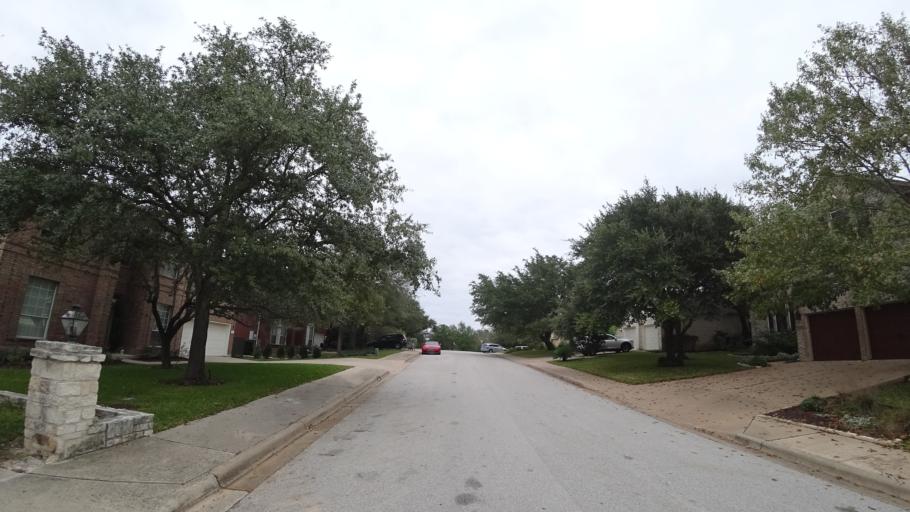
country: US
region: Texas
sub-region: Travis County
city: Bee Cave
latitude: 30.3116
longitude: -97.9236
